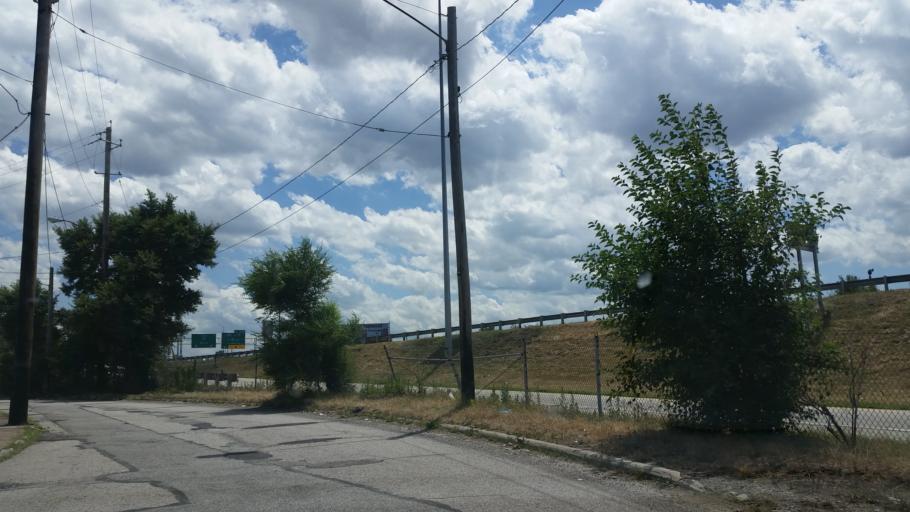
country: US
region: Ohio
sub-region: Cuyahoga County
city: Cleveland
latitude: 41.4900
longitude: -81.6656
